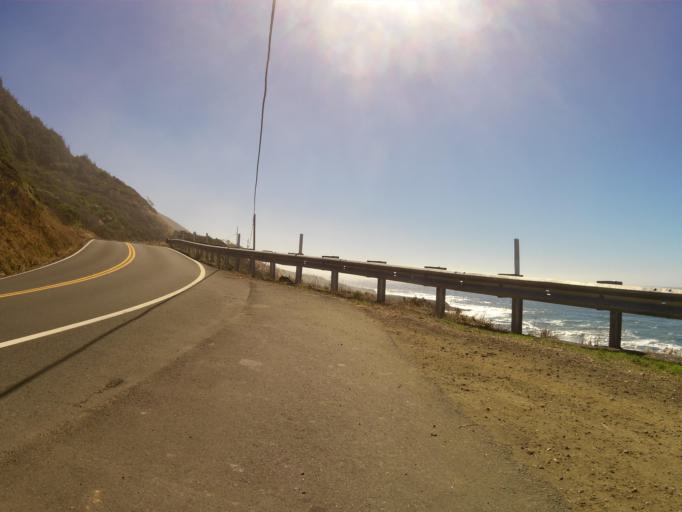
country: US
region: California
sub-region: Mendocino County
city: Fort Bragg
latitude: 39.6127
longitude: -123.7822
